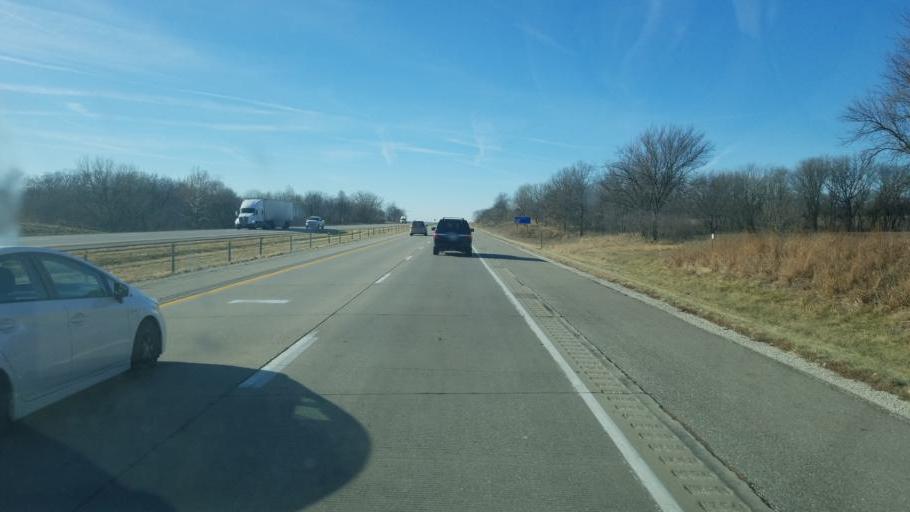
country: US
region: Iowa
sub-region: Dallas County
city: Van Meter
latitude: 41.5518
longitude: -93.9373
